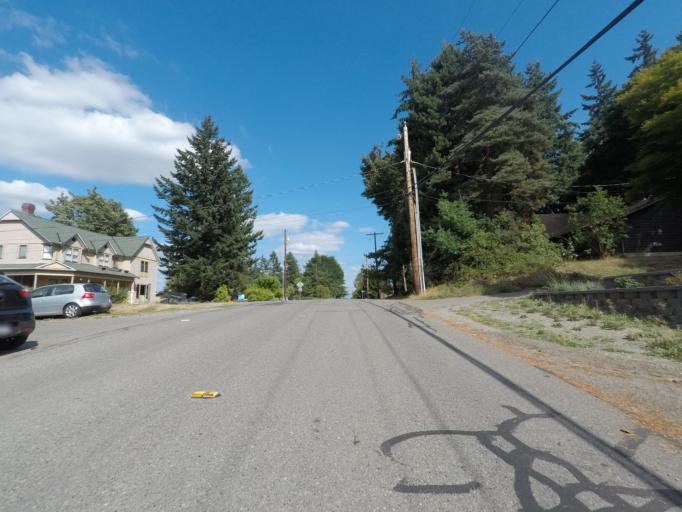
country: US
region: Washington
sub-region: King County
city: Kenmore
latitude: 47.7707
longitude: -122.2577
